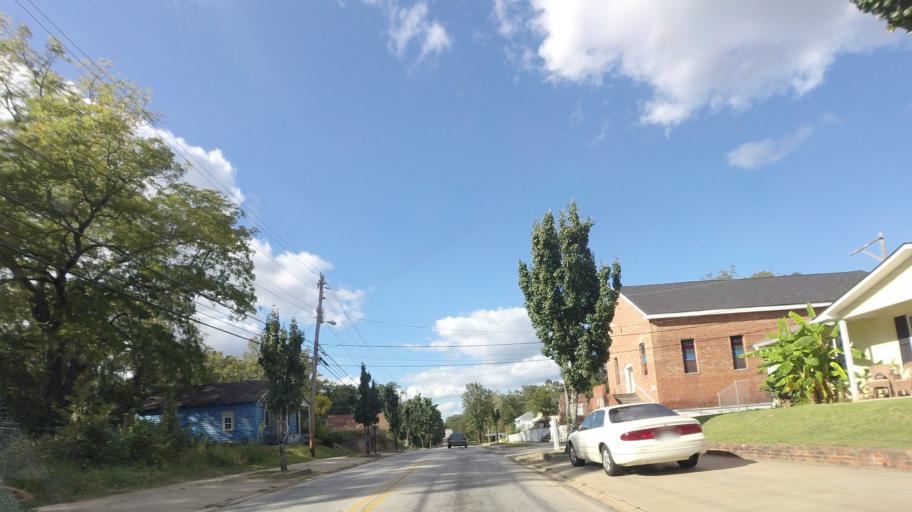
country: US
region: Georgia
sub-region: Lamar County
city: Barnesville
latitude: 33.0578
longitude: -84.1554
